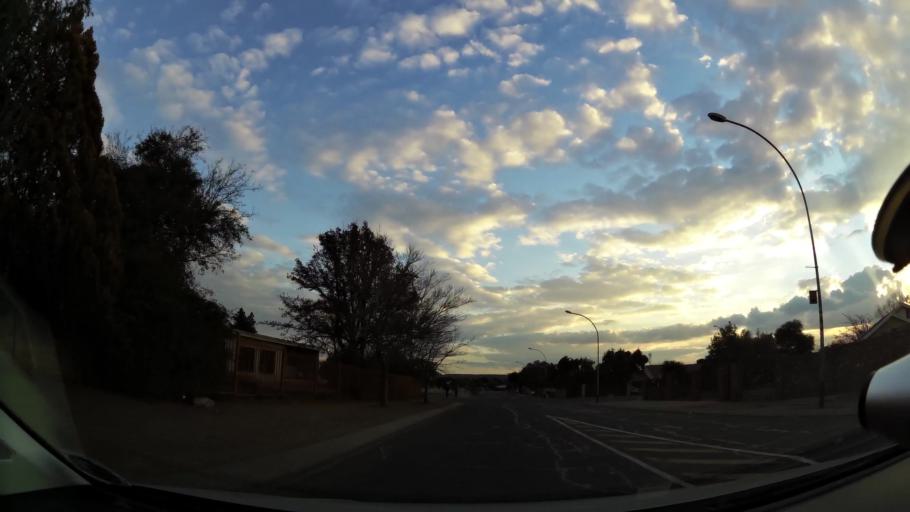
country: ZA
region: Orange Free State
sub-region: Mangaung Metropolitan Municipality
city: Bloemfontein
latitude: -29.1603
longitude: 26.1892
